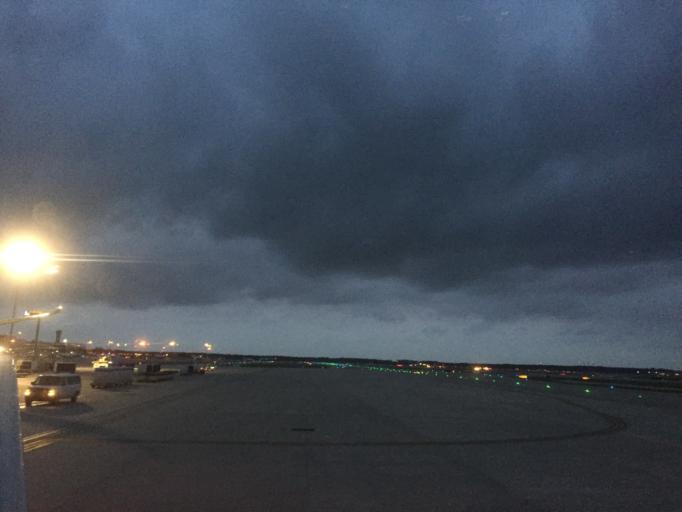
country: US
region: Texas
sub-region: Harris County
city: Aldine
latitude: 29.9904
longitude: -95.3404
